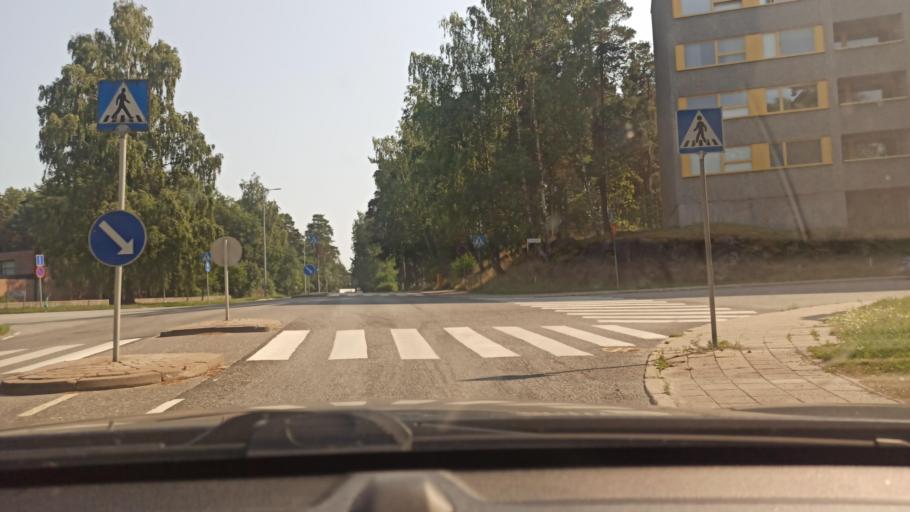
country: FI
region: Varsinais-Suomi
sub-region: Turku
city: Turku
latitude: 60.4633
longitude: 22.2171
